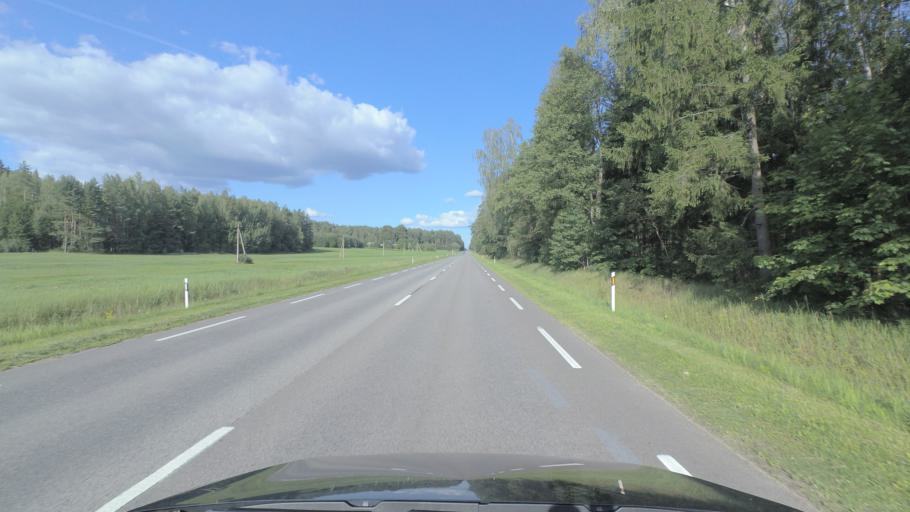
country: LT
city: Pabrade
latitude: 54.9620
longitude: 25.6998
